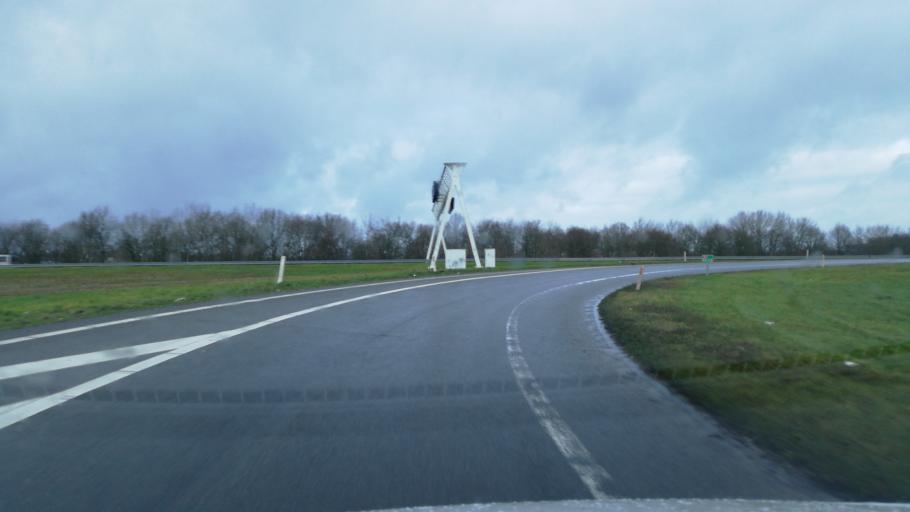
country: NL
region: Gelderland
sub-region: Gemeente Apeldoorn
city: Beekbergen
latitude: 52.1740
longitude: 5.9782
